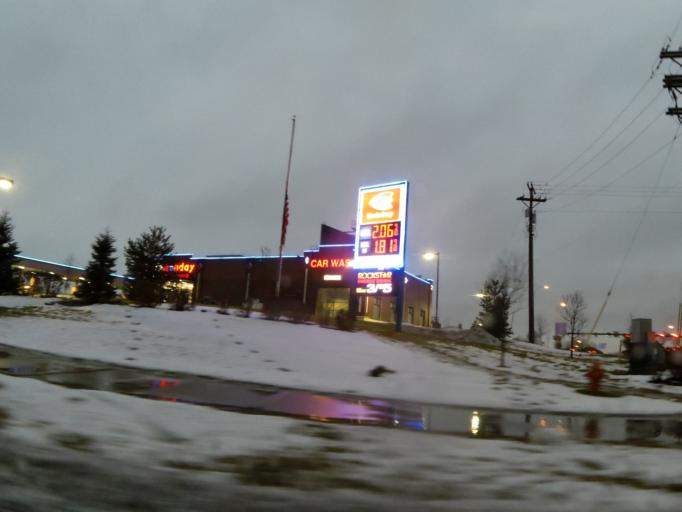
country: US
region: Minnesota
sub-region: Olmsted County
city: Rochester
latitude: 44.0434
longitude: -92.4858
